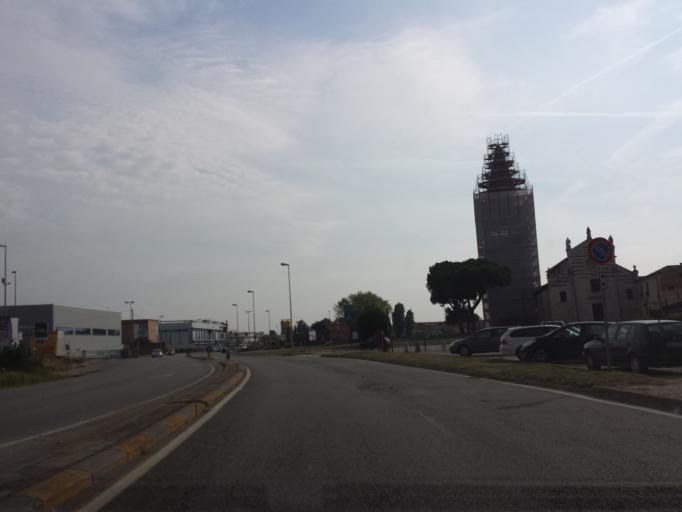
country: IT
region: Veneto
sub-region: Provincia di Verona
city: Soave
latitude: 45.4031
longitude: 11.2628
